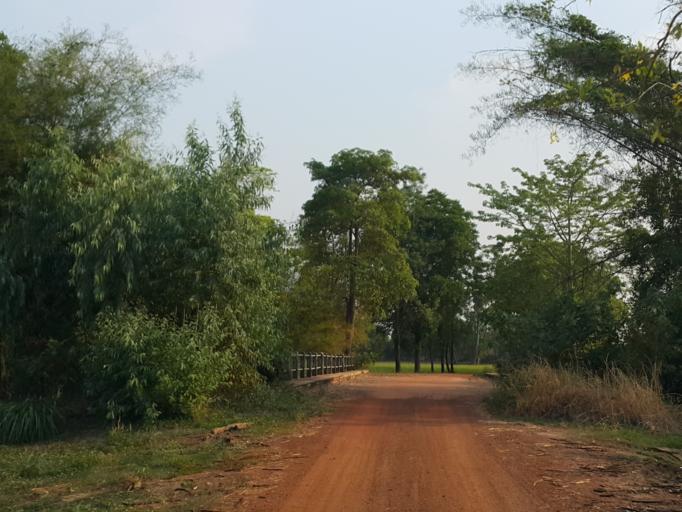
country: TH
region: Uthai Thani
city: Huai Khot
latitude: 15.3175
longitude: 99.6732
